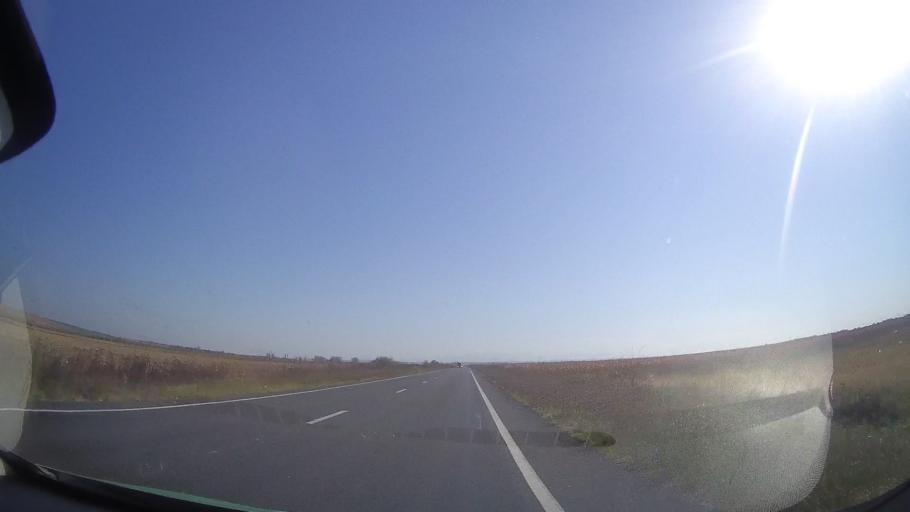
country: RO
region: Timis
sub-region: Comuna Belint
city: Belint
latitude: 45.7455
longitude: 21.8008
